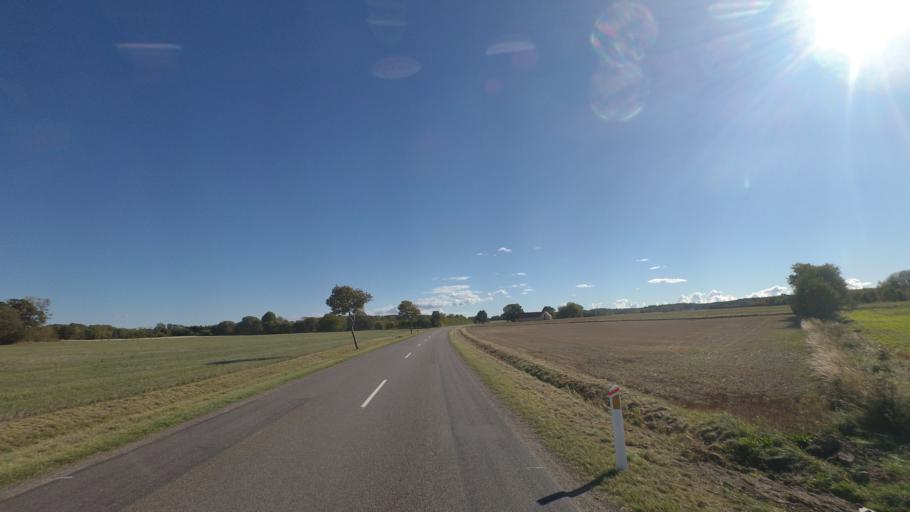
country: DK
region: Capital Region
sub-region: Bornholm Kommune
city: Nexo
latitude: 55.1144
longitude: 15.1085
